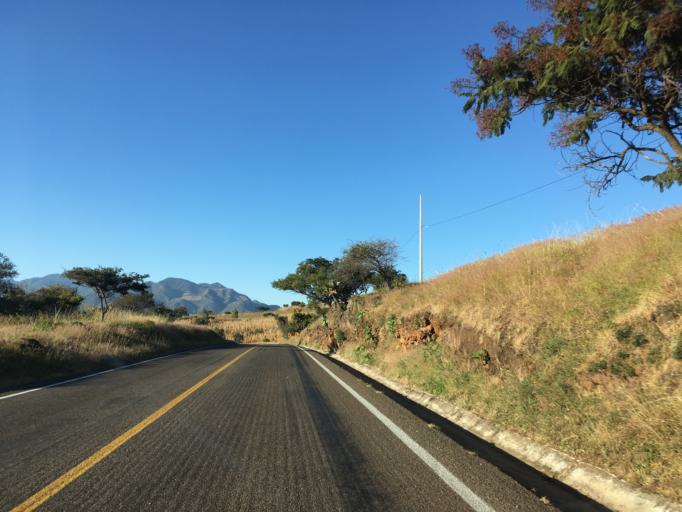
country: MX
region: Michoacan
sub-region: Tuxpan
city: La Soledad
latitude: 19.5124
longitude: -100.4695
